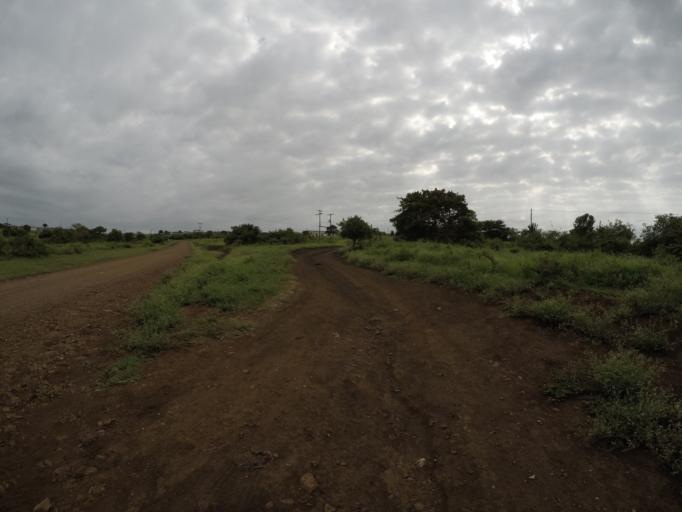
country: ZA
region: KwaZulu-Natal
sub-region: uThungulu District Municipality
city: Empangeni
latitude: -28.6411
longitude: 31.9049
